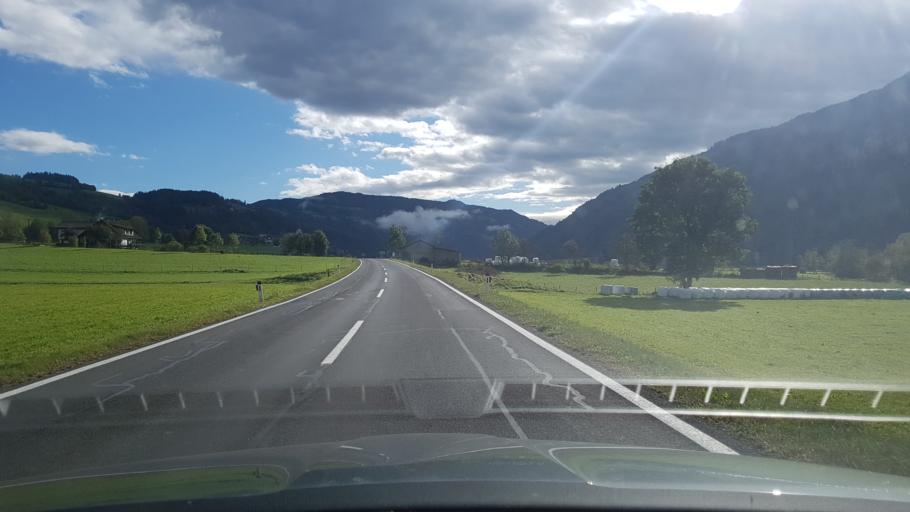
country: AT
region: Styria
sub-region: Politischer Bezirk Murau
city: Sankt Peter am Kammersberg
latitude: 47.1877
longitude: 14.1683
